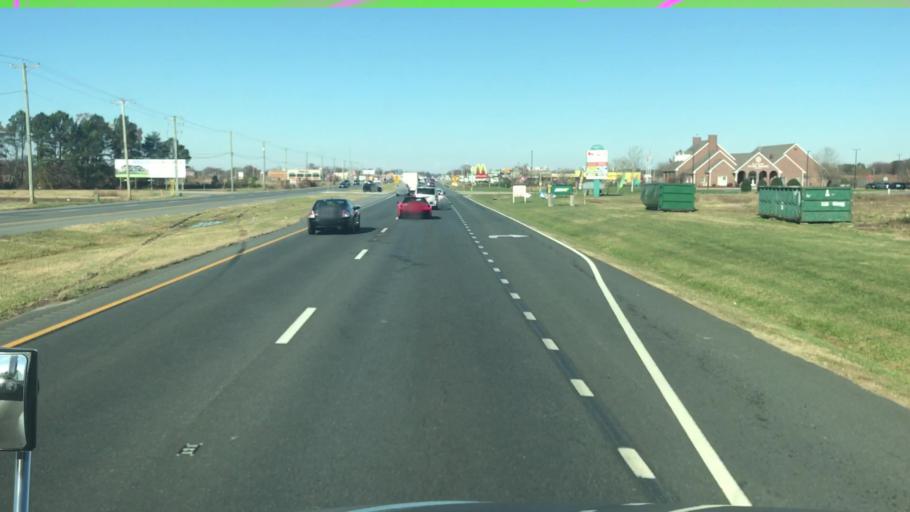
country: US
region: Delaware
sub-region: Sussex County
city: Bridgeville
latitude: 38.7180
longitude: -75.5896
